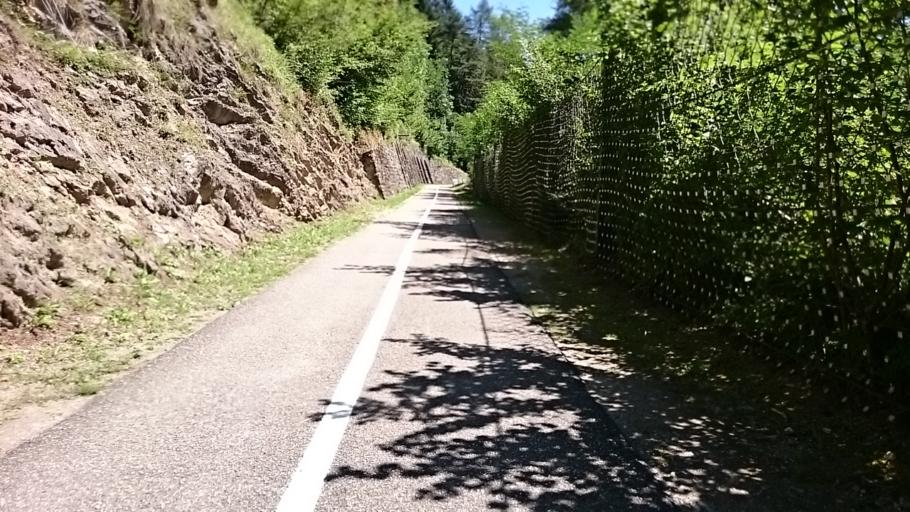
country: IT
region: Veneto
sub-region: Provincia di Belluno
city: Valle di Cadore
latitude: 46.4169
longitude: 12.3182
